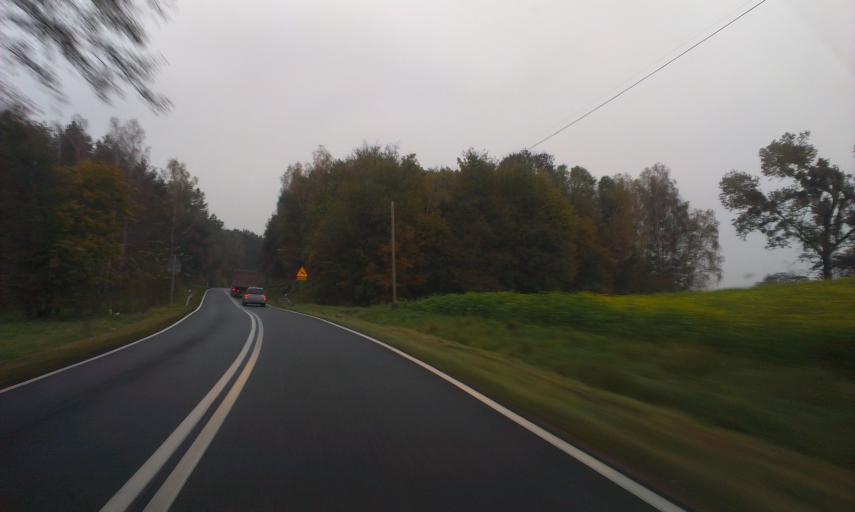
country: PL
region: Kujawsko-Pomorskie
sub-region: Powiat sepolenski
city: Sosno
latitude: 53.4396
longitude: 17.6479
